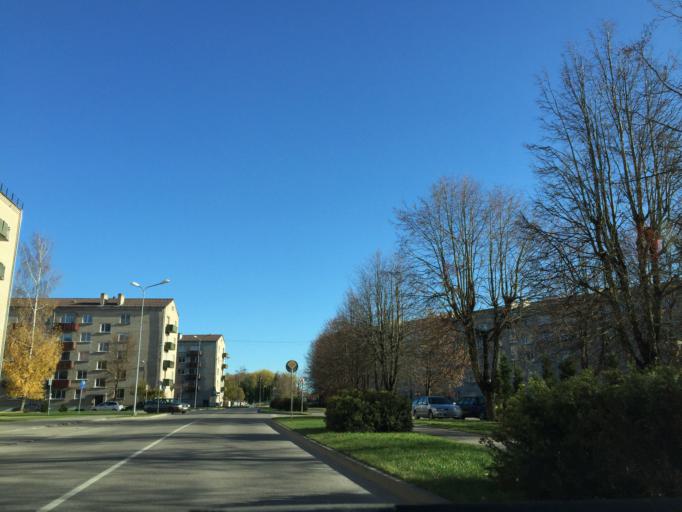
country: LV
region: Aizkraukles Rajons
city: Aizkraukle
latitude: 56.6006
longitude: 25.2570
